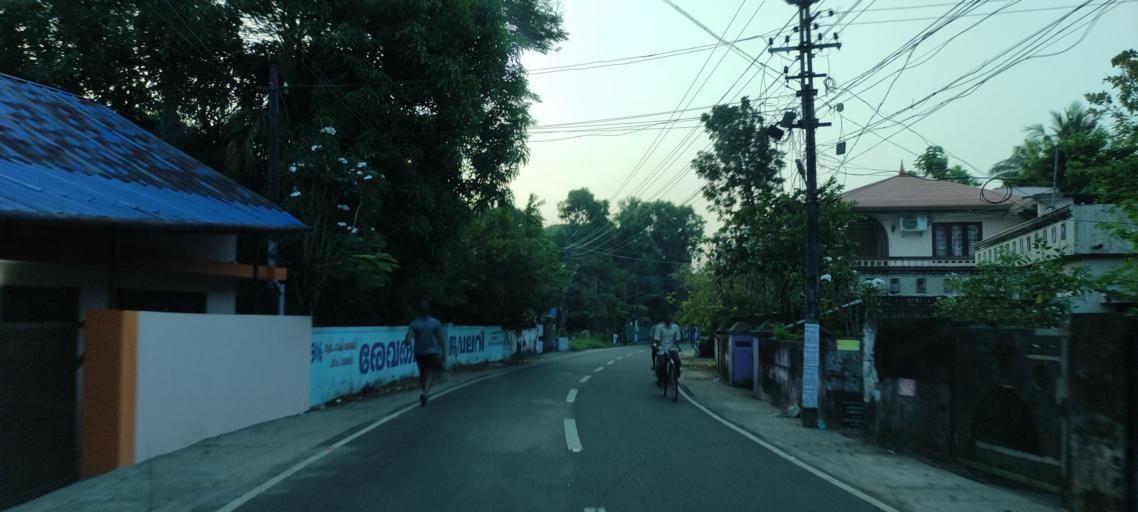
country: IN
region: Kerala
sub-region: Alappuzha
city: Alleppey
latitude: 9.4640
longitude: 76.3434
